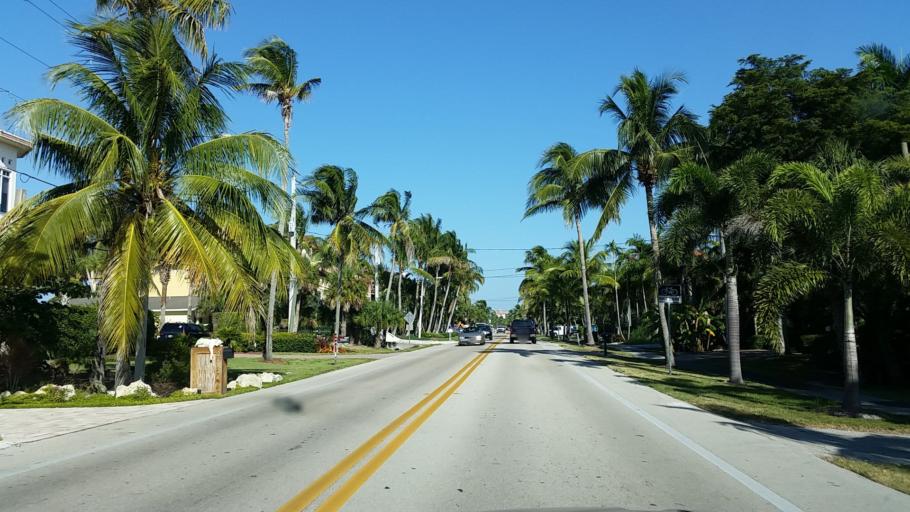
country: US
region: Florida
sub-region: Lee County
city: Bonita Springs
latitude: 26.3454
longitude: -81.8513
